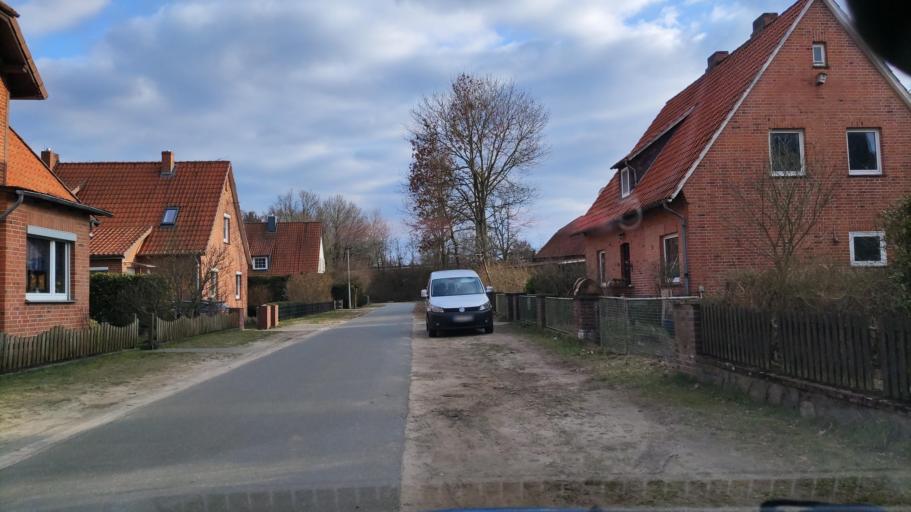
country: DE
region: Lower Saxony
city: Jelmstorf
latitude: 53.1102
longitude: 10.5401
